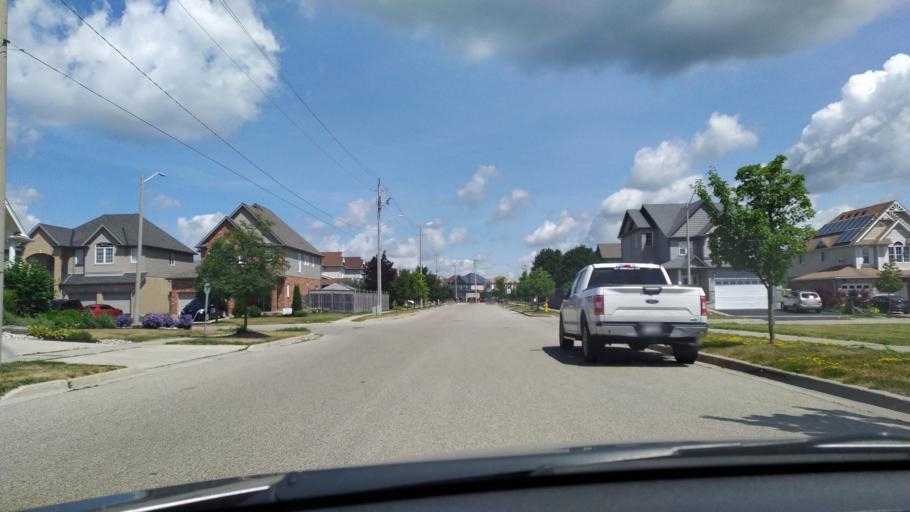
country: CA
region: Ontario
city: Kitchener
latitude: 43.4051
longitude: -80.6730
